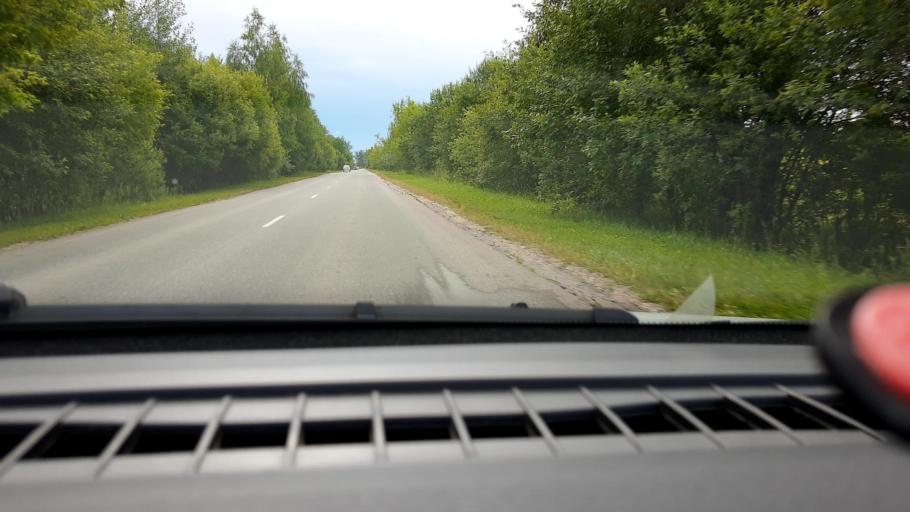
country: RU
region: Nizjnij Novgorod
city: Kstovo
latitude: 56.1499
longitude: 44.2990
